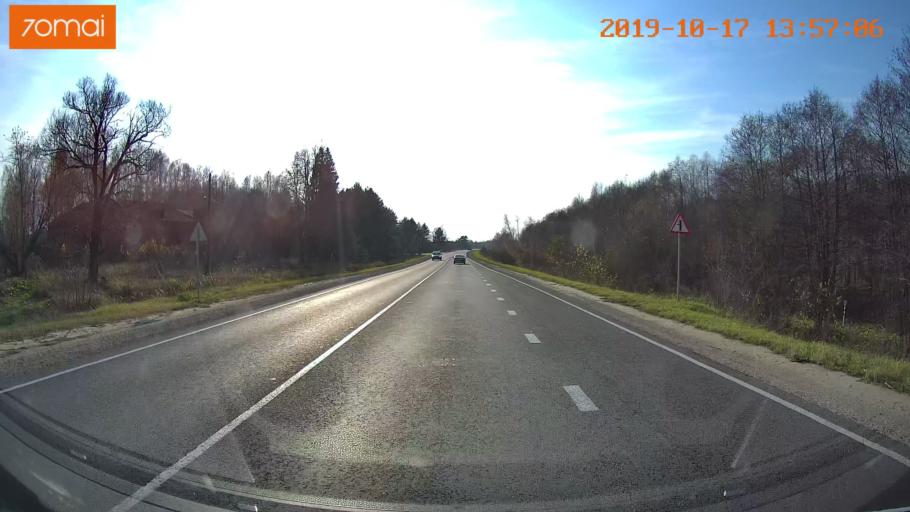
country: RU
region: Rjazan
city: Spas-Klepiki
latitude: 55.1465
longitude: 40.2528
